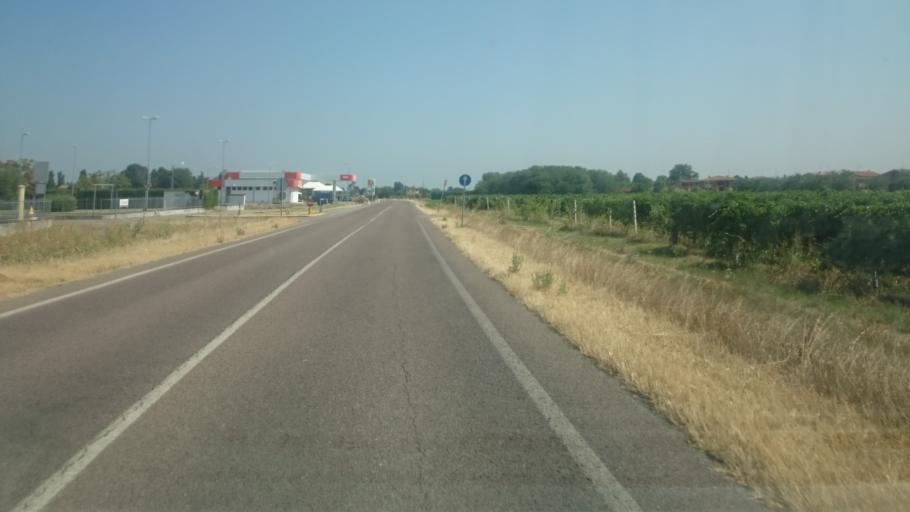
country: IT
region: Emilia-Romagna
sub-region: Provincia di Reggio Emilia
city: Arceto
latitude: 44.6183
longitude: 10.7119
